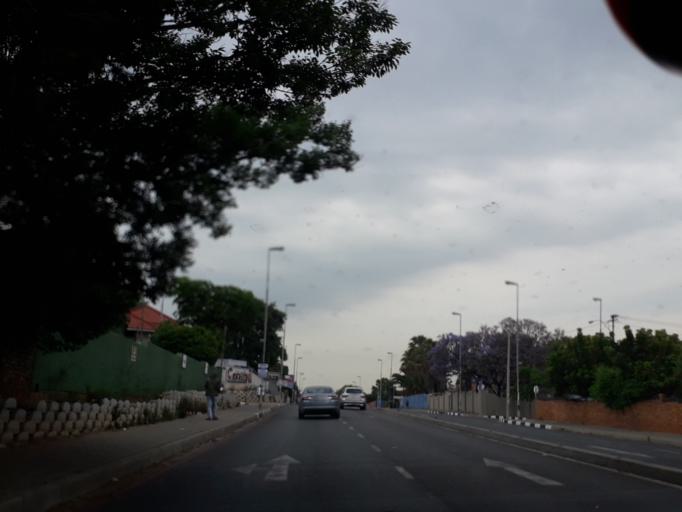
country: ZA
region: Gauteng
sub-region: City of Johannesburg Metropolitan Municipality
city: Johannesburg
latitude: -26.1413
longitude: 28.0867
